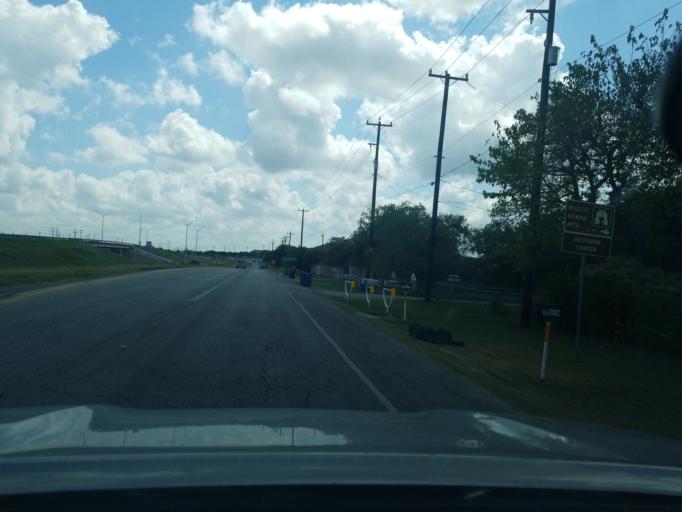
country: US
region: Texas
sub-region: Bexar County
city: San Antonio
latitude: 29.3196
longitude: -98.5057
